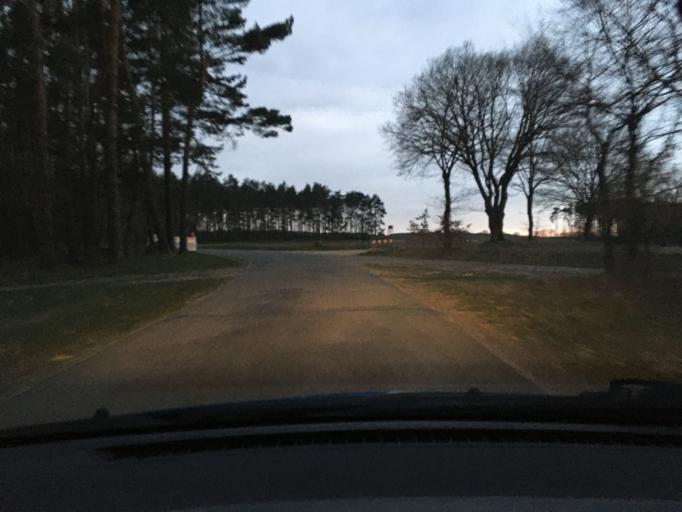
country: DE
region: Lower Saxony
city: Neetze
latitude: 53.2435
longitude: 10.6232
